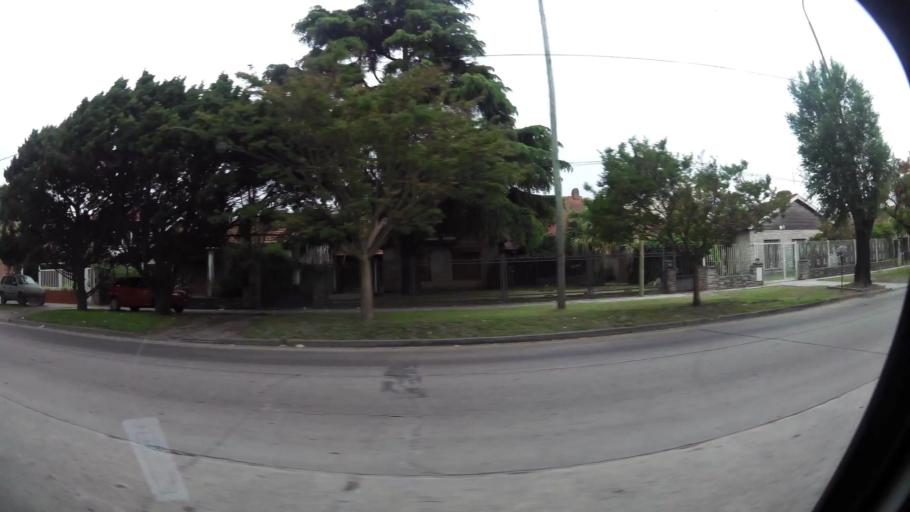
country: AR
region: Buenos Aires
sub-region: Partido de La Plata
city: La Plata
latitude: -34.8954
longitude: -57.9880
